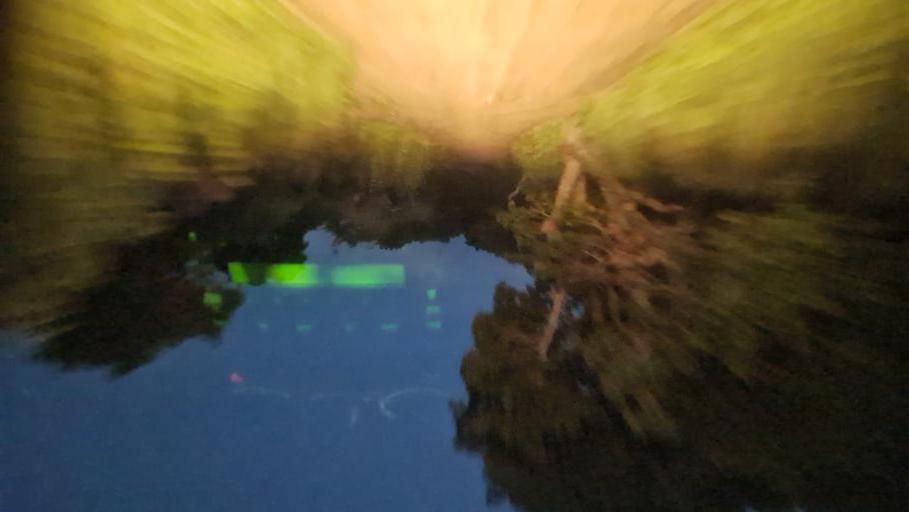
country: MZ
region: Nampula
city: Nampula
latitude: -14.6714
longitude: 39.8342
